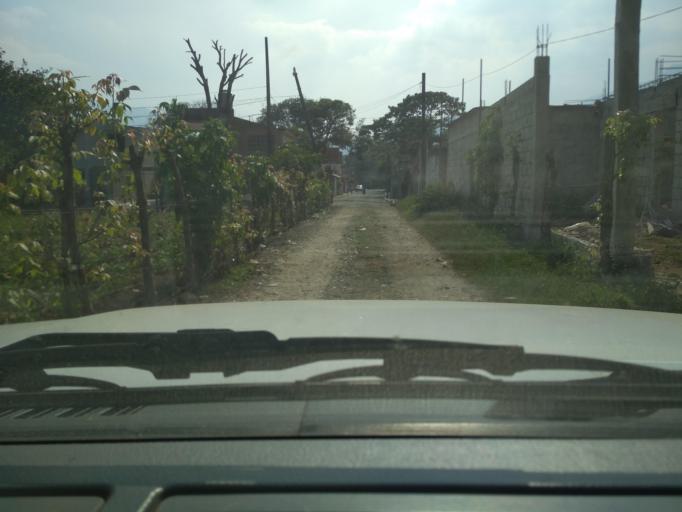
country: MX
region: Veracruz
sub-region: Mariano Escobedo
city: Palmira
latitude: 18.8716
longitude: -97.0944
